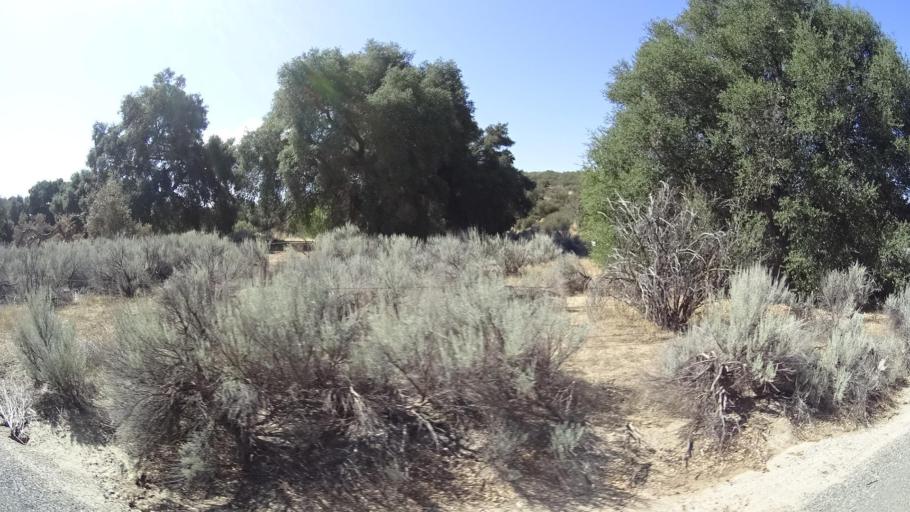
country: US
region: California
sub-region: San Diego County
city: Julian
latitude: 33.2881
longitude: -116.6500
